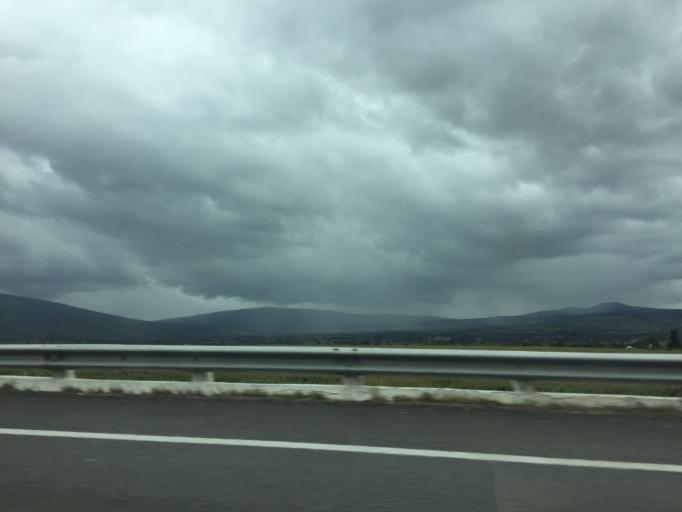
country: MX
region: Jalisco
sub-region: Zapotlanejo
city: La Mezquitera
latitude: 20.5578
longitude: -103.0680
